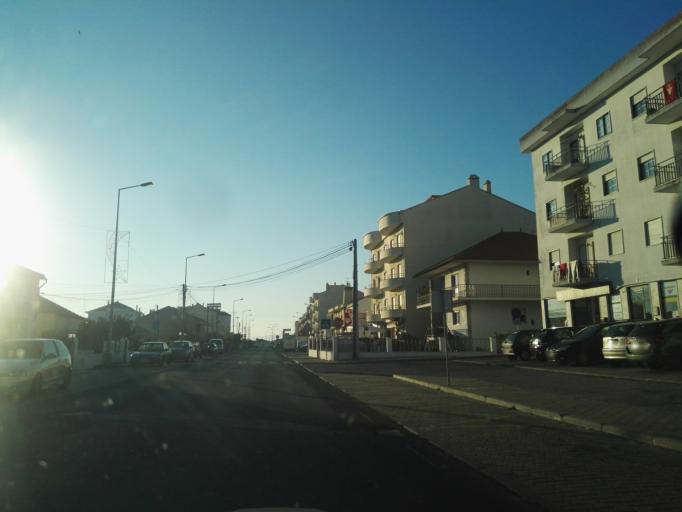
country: PT
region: Santarem
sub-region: Benavente
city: Samora Correia
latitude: 38.9247
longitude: -8.8853
